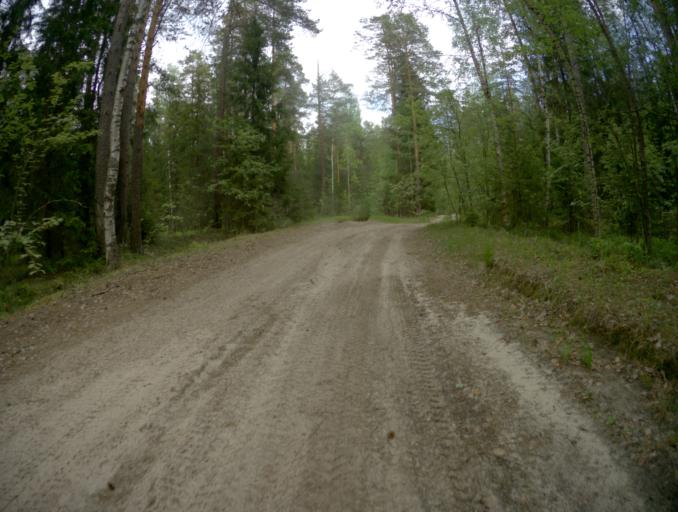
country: RU
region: Vladimir
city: Ivanishchi
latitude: 55.7503
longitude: 40.3837
